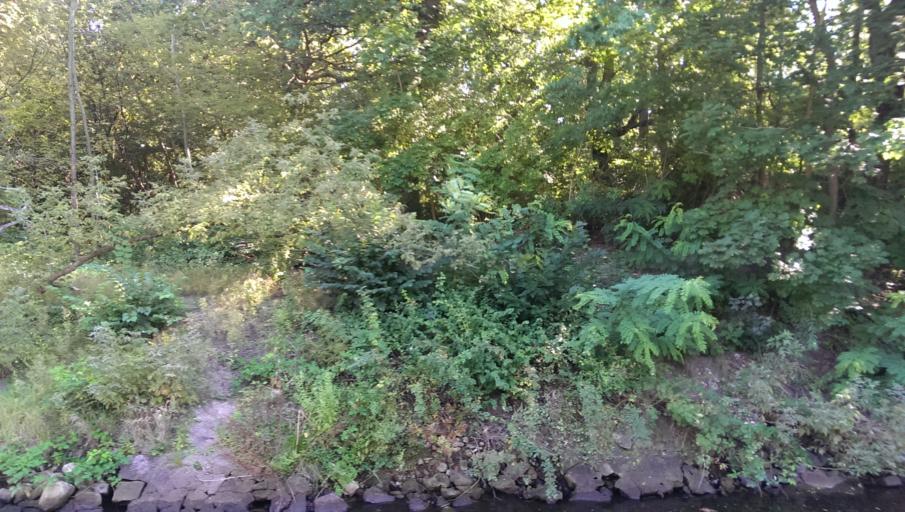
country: DE
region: Berlin
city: Wannsee
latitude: 52.4065
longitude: 13.1412
